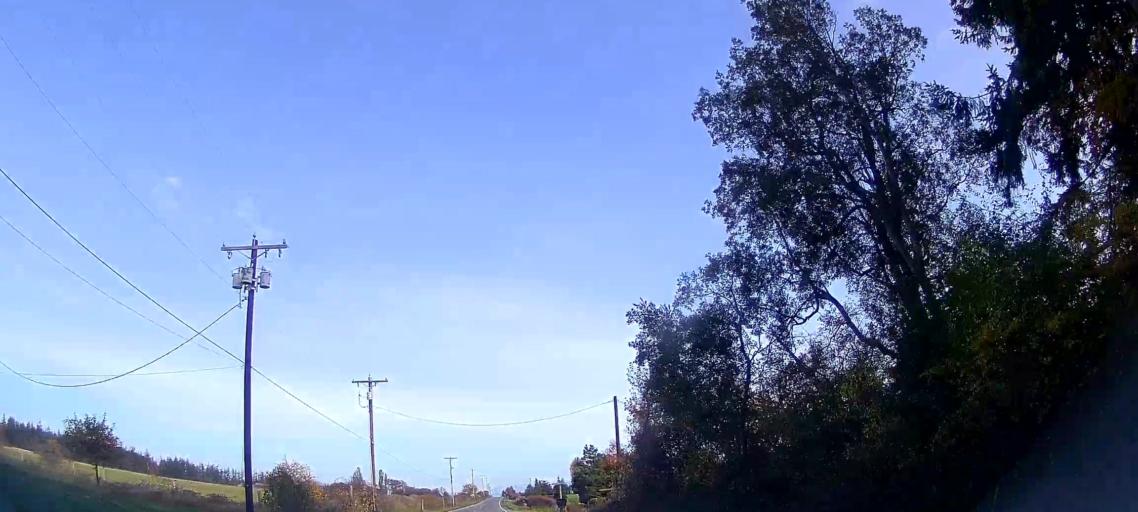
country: US
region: Washington
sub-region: Snohomish County
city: Stanwood
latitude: 48.2546
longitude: -122.4504
